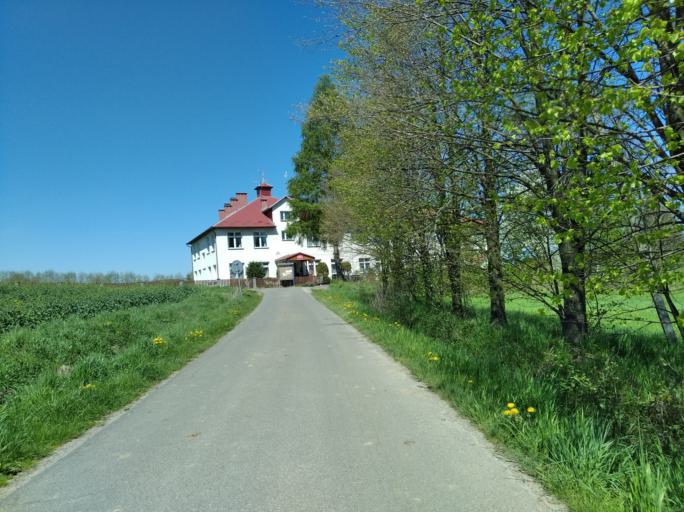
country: PL
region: Subcarpathian Voivodeship
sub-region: Powiat ropczycko-sedziszowski
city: Wielopole Skrzynskie
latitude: 49.9153
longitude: 21.5465
